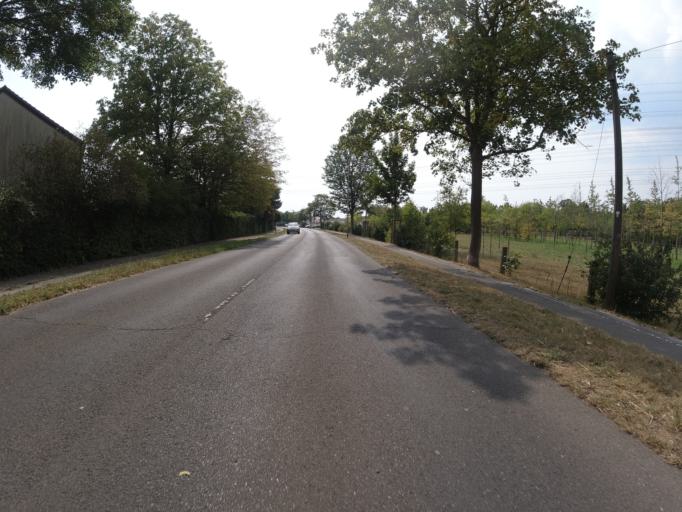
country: DE
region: North Rhine-Westphalia
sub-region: Regierungsbezirk Dusseldorf
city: Moers
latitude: 51.3963
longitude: 6.6439
